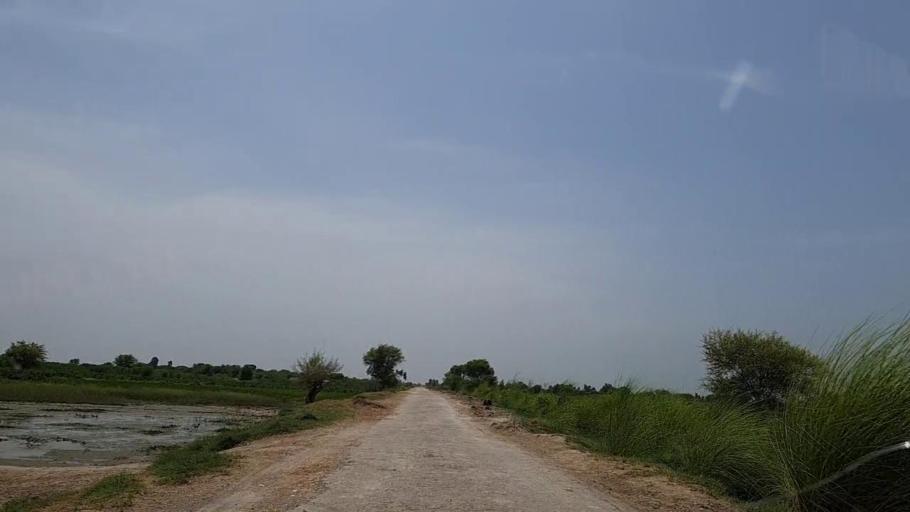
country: PK
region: Sindh
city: Khanpur
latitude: 27.8801
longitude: 69.4922
